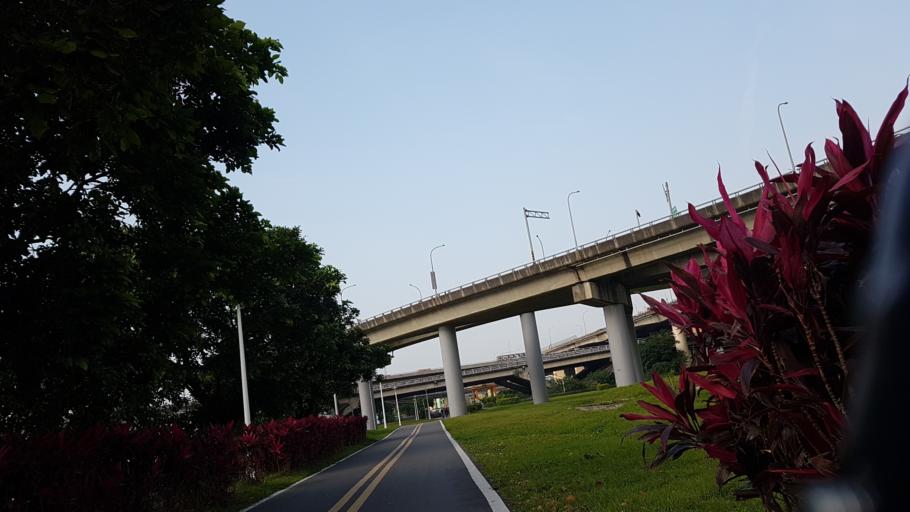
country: TW
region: Taipei
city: Taipei
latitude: 25.0478
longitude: 121.5037
